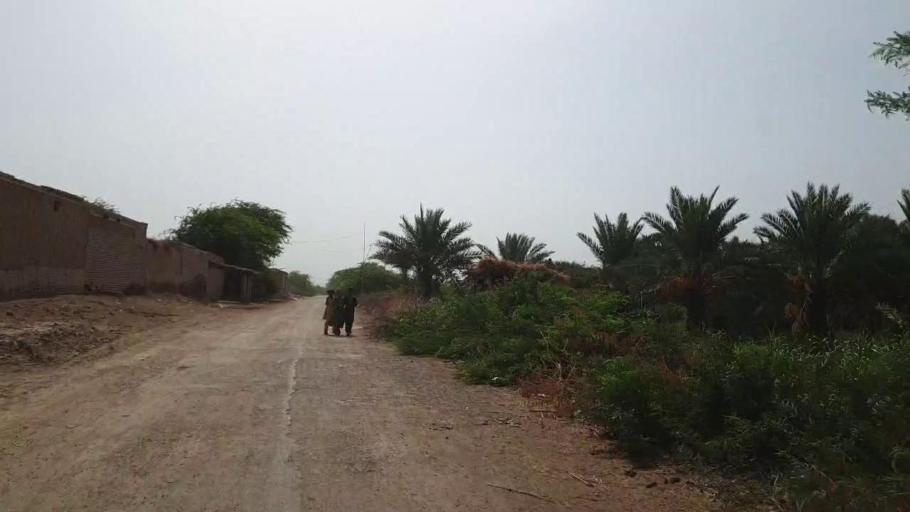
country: PK
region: Sindh
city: Bandhi
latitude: 26.5713
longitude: 68.3735
